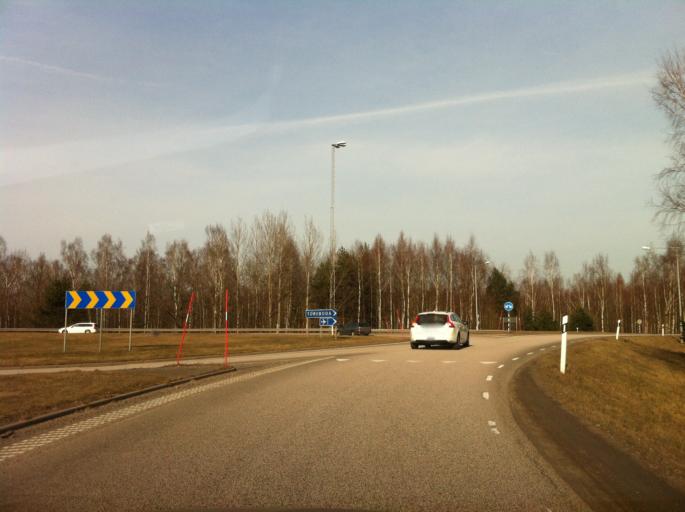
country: SE
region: Vaestra Goetaland
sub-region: Skovde Kommun
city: Skoevde
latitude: 58.4197
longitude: 13.8860
